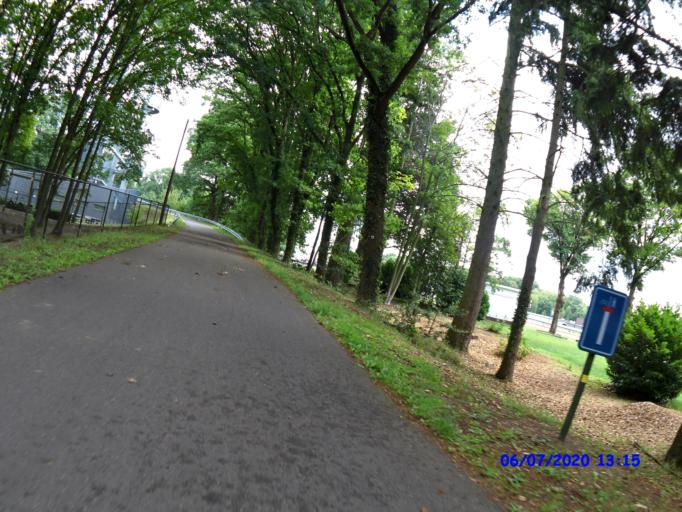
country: BE
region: Flanders
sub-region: Provincie Antwerpen
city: Dessel
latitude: 51.2343
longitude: 5.1627
